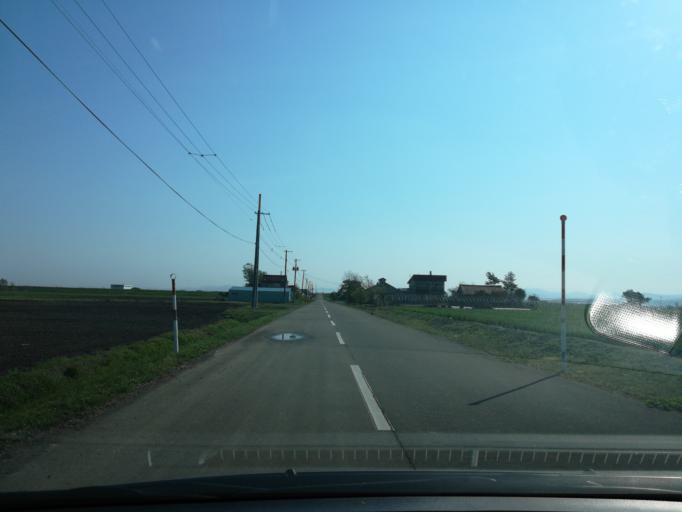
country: JP
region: Hokkaido
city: Iwamizawa
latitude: 43.1289
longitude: 141.6722
